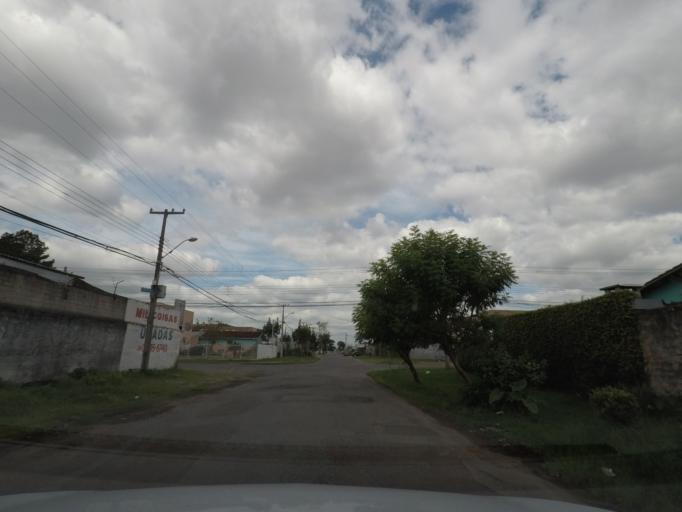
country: BR
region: Parana
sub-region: Sao Jose Dos Pinhais
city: Sao Jose dos Pinhais
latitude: -25.4863
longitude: -49.2396
